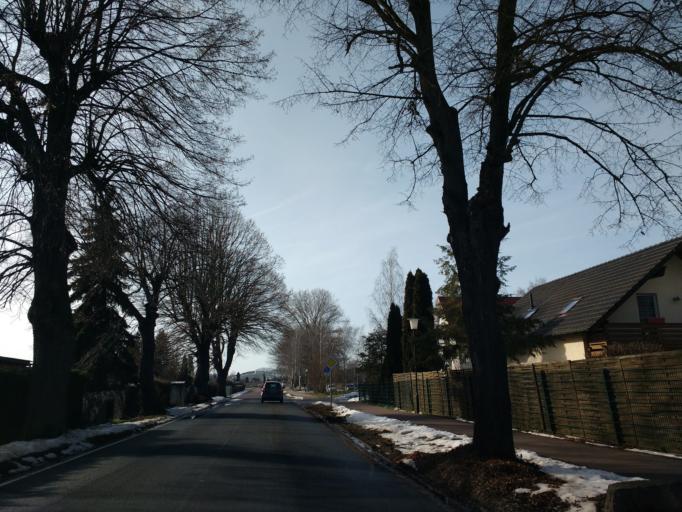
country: DE
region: Saxony-Anhalt
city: Gutenberg
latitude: 51.5462
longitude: 11.9650
